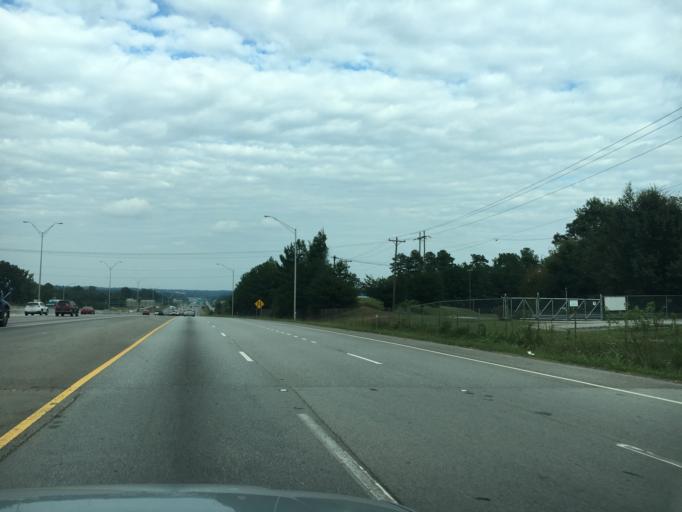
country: US
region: South Carolina
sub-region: Greenville County
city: Gantt
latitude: 34.7913
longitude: -82.4137
